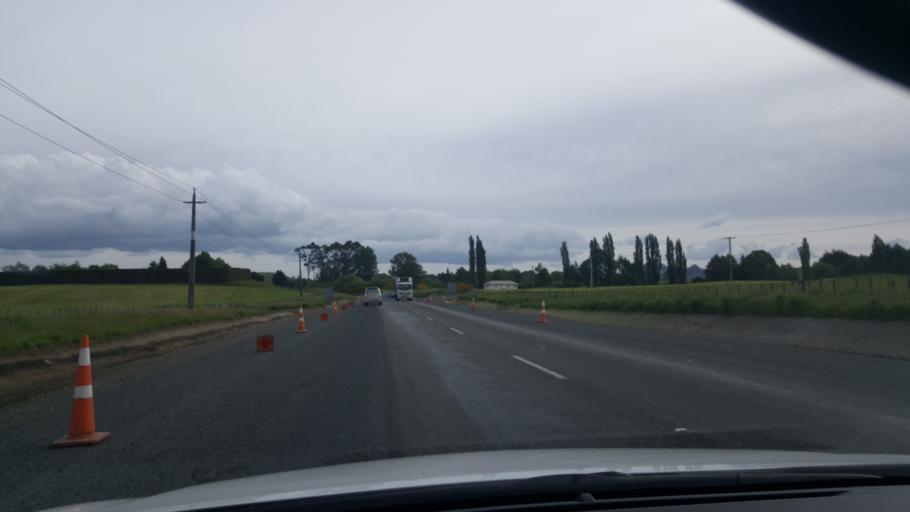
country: NZ
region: Bay of Plenty
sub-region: Rotorua District
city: Rotorua
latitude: -38.4114
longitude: 176.3217
